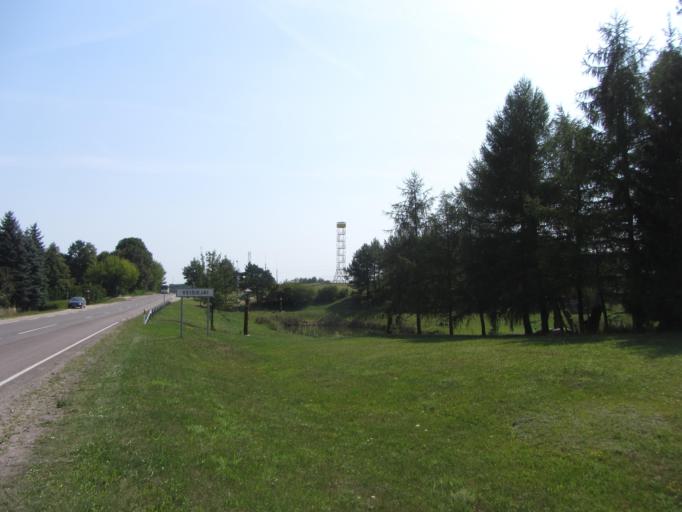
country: LT
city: Veisiejai
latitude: 54.1051
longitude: 23.6757
